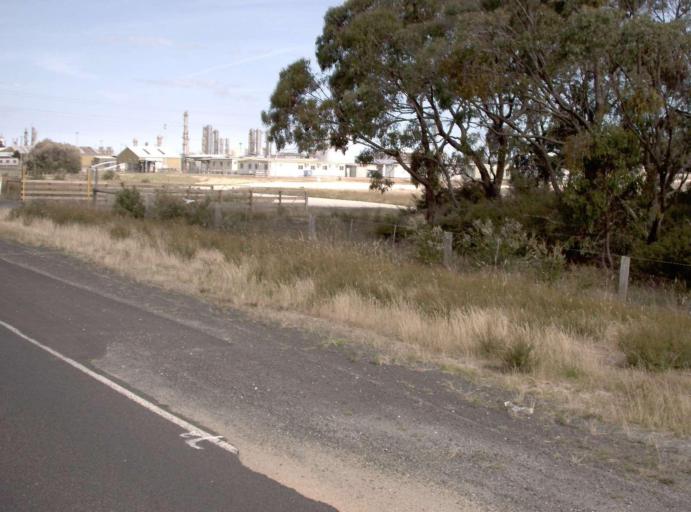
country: AU
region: Victoria
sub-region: Wellington
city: Sale
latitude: -38.2199
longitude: 147.1601
